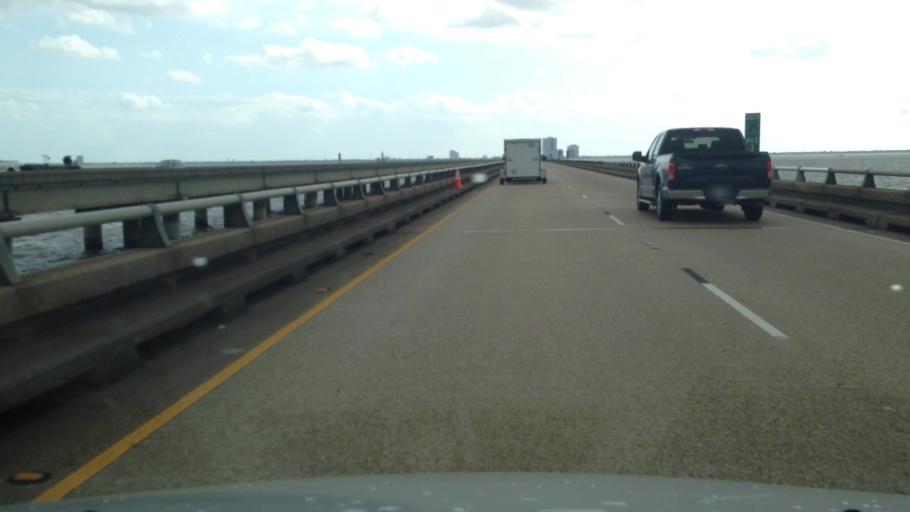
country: US
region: Louisiana
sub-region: Jefferson Parish
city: Metairie
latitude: 30.0665
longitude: -90.1463
